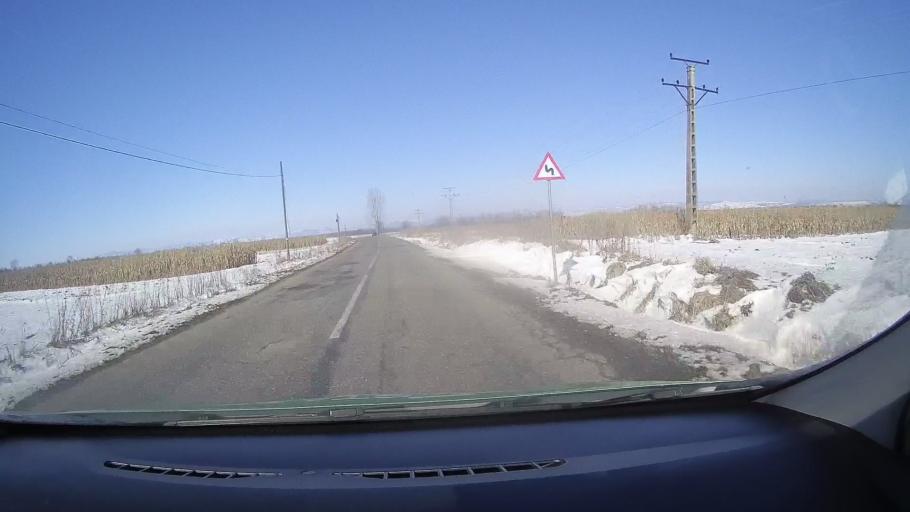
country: RO
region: Brasov
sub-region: Comuna Harseni
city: Harseni
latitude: 45.7642
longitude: 25.0058
